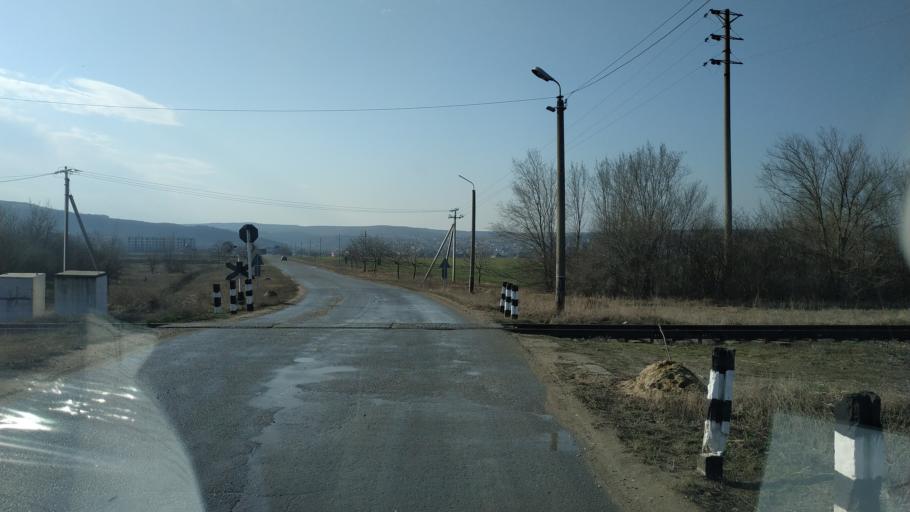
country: MD
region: Chisinau
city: Singera
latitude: 46.6933
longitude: 29.0539
